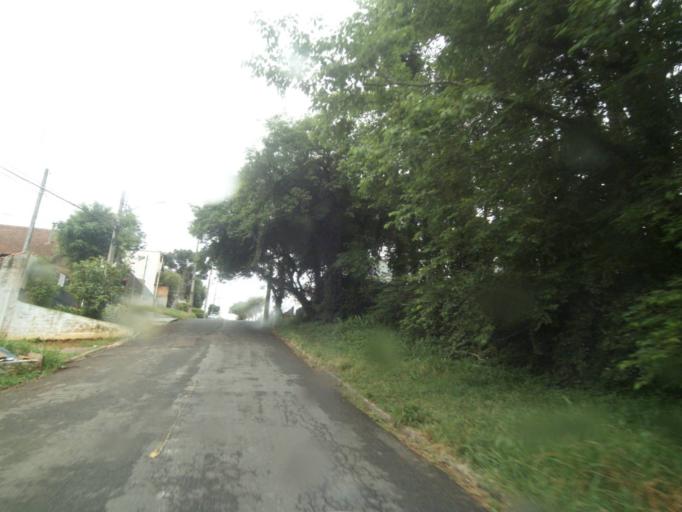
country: BR
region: Parana
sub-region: Curitiba
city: Curitiba
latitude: -25.4284
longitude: -49.3267
